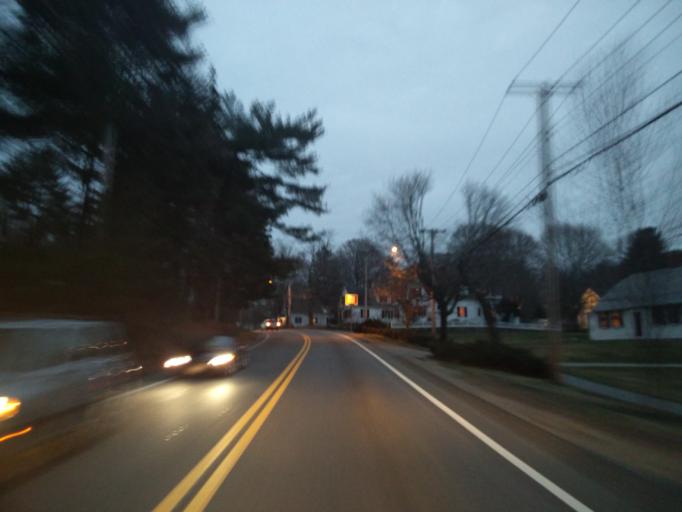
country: US
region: Massachusetts
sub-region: Plymouth County
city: Hingham
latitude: 42.2193
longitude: -70.8858
